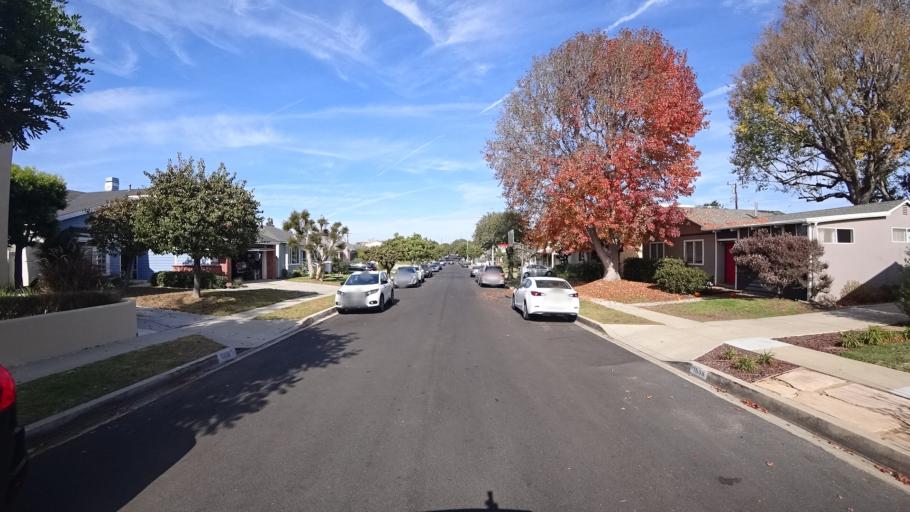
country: US
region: California
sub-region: Los Angeles County
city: Del Aire
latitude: 33.8904
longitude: -118.3826
